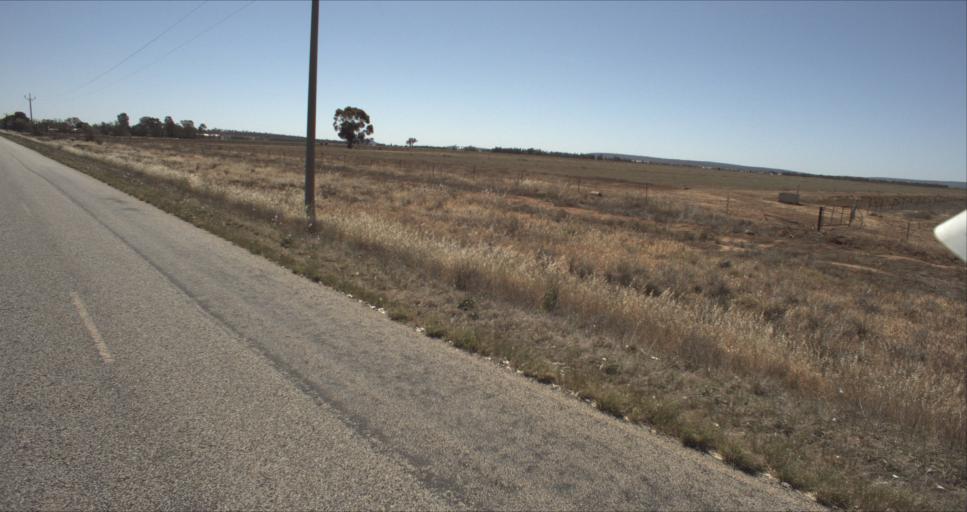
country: AU
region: New South Wales
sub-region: Leeton
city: Leeton
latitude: -34.4462
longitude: 146.2969
